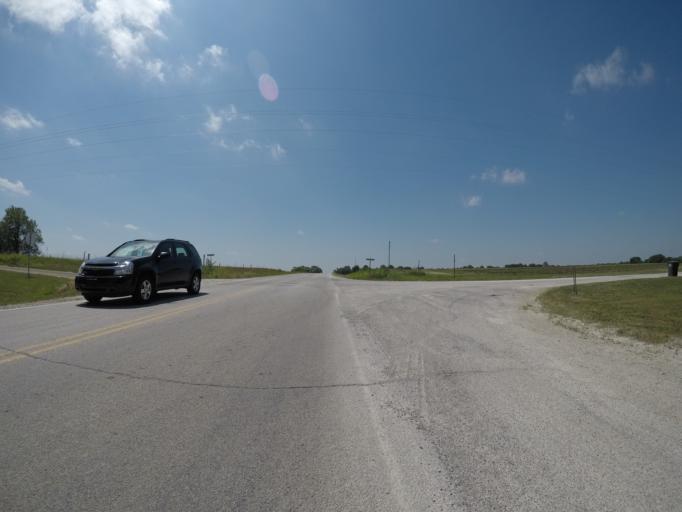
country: US
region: Kansas
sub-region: Pottawatomie County
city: Westmoreland
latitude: 39.3196
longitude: -96.4361
